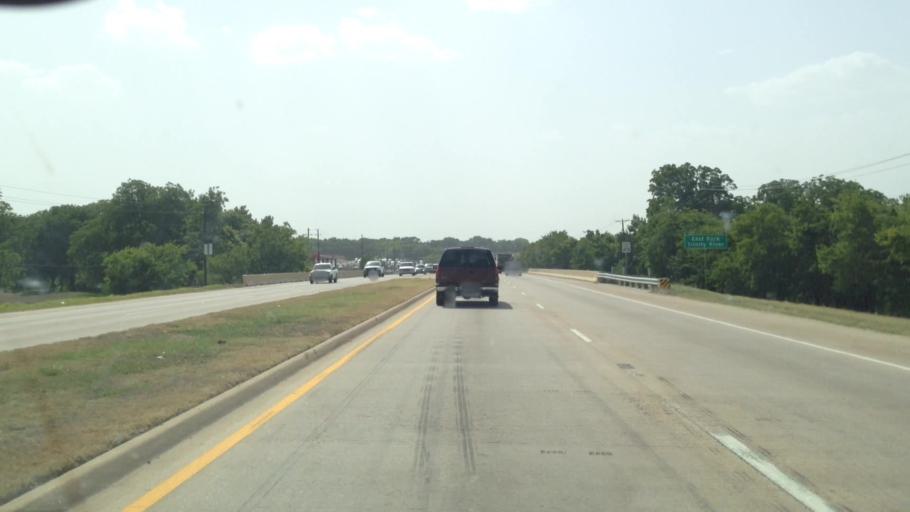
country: US
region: Texas
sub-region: Collin County
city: McKinney
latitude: 33.2033
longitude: -96.5945
